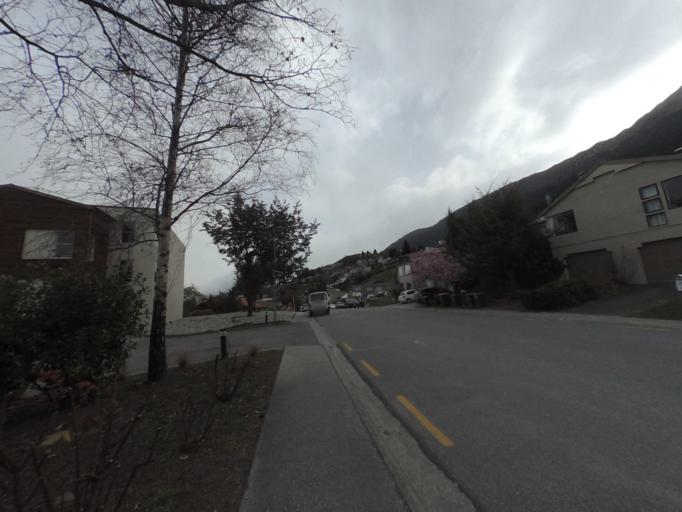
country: NZ
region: Otago
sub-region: Queenstown-Lakes District
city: Queenstown
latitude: -45.0387
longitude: 168.6384
